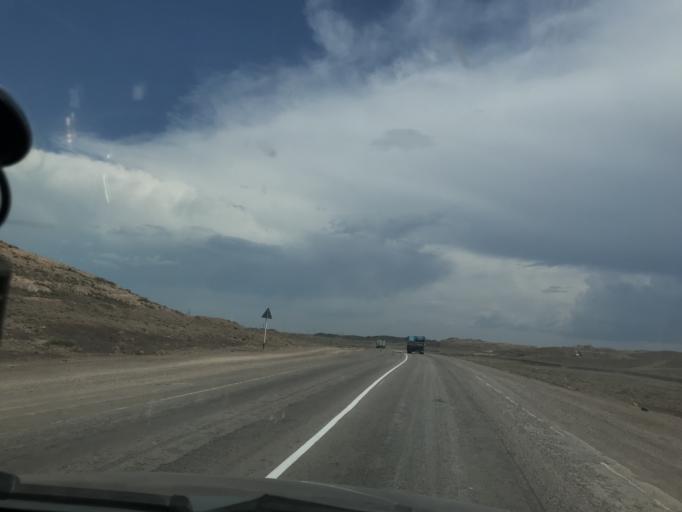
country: KZ
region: Zhambyl
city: Mynaral
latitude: 45.3696
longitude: 73.6593
